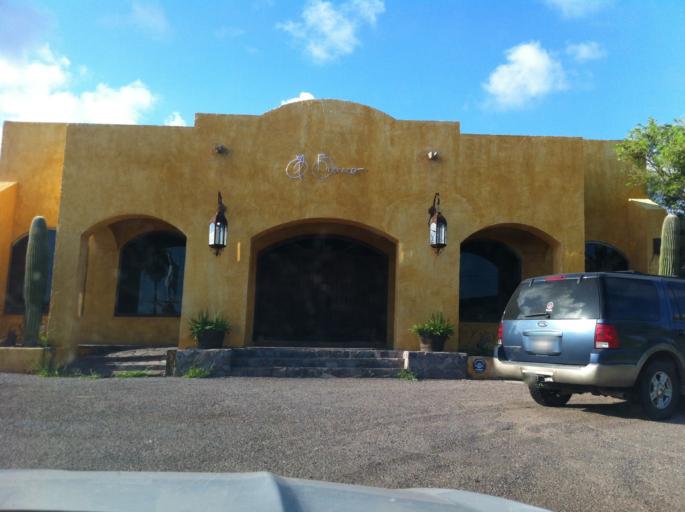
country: MX
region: Sonora
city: Heroica Guaymas
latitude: 27.9596
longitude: -111.0369
